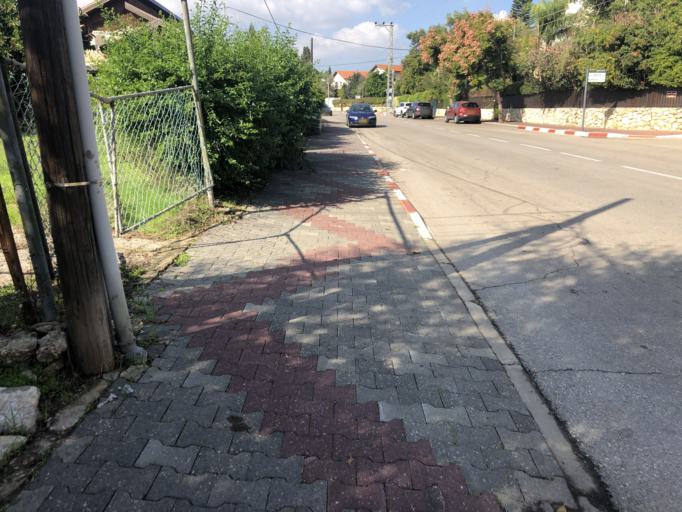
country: IL
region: Tel Aviv
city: Or Yehuda
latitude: 32.0316
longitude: 34.8732
